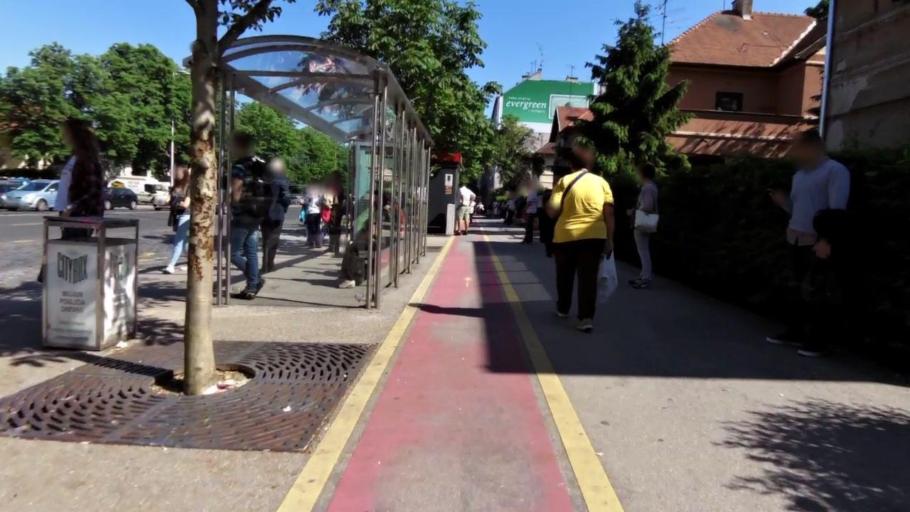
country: HR
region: Grad Zagreb
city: Zagreb
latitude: 45.8130
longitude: 15.9987
